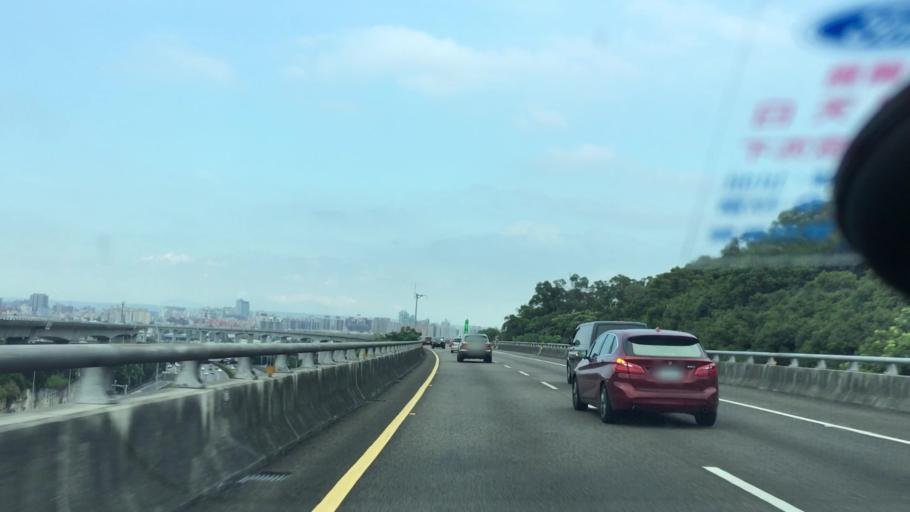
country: TW
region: Taiwan
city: Daxi
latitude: 24.9318
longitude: 121.1851
